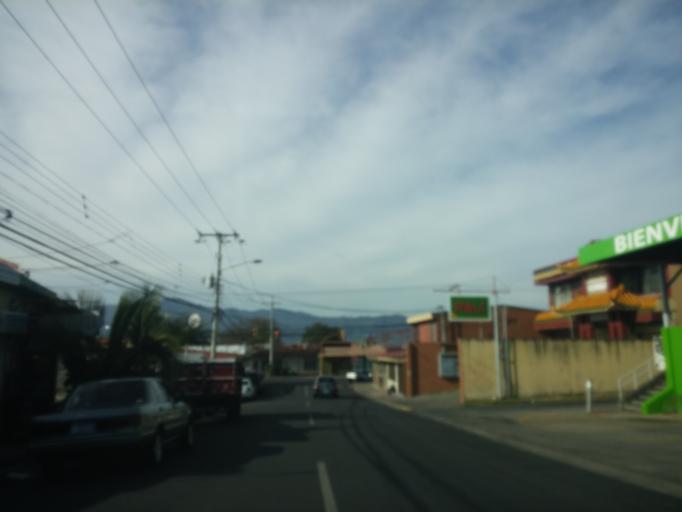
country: CR
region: Heredia
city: Llorente
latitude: 10.0018
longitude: -84.1530
